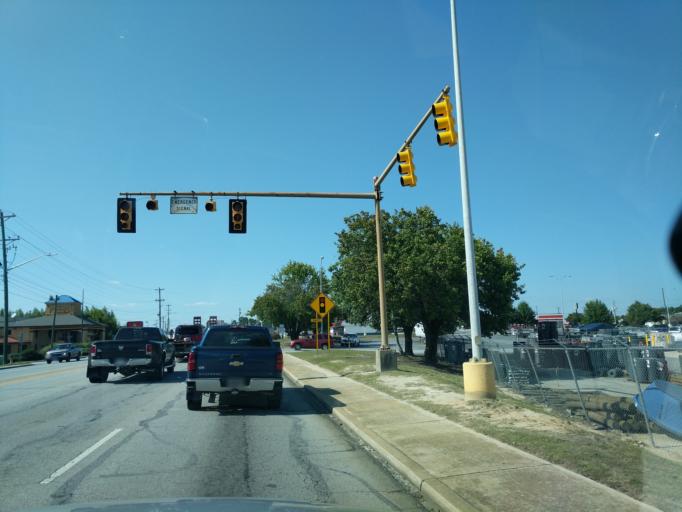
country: US
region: South Carolina
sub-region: Newberry County
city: Newberry
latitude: 34.2809
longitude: -81.5948
